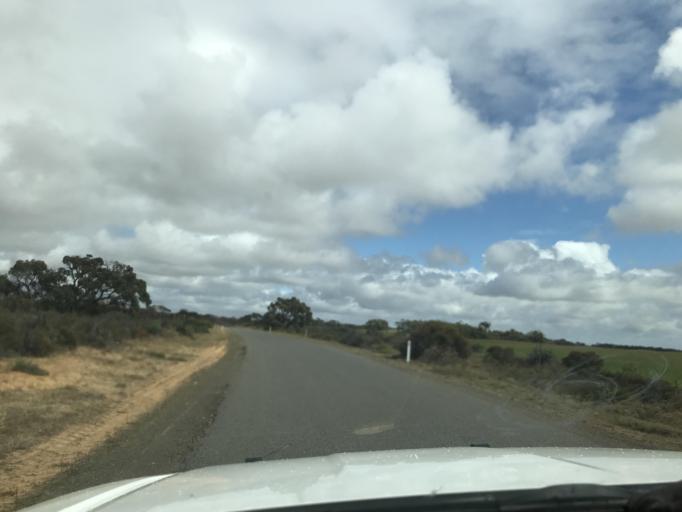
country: AU
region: South Australia
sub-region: Tatiara
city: Bordertown
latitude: -36.1789
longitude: 141.1572
